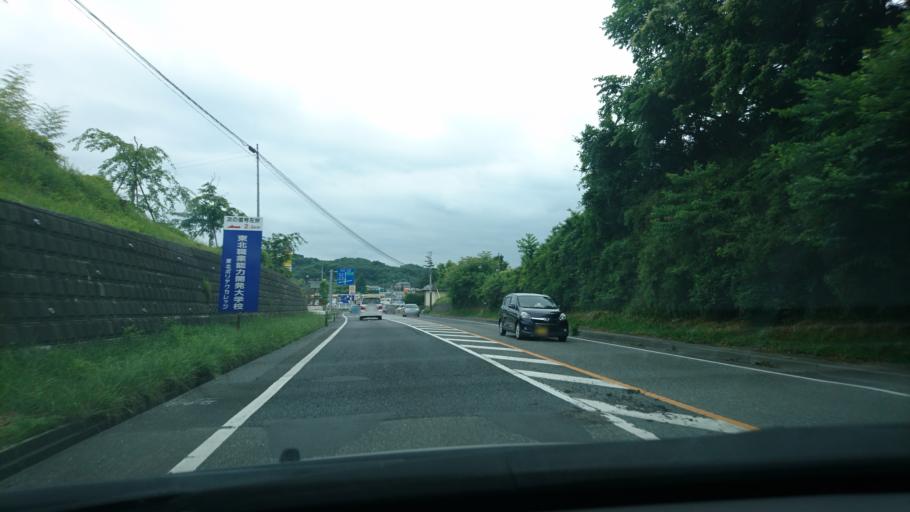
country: JP
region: Miyagi
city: Furukawa
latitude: 38.7149
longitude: 141.0214
